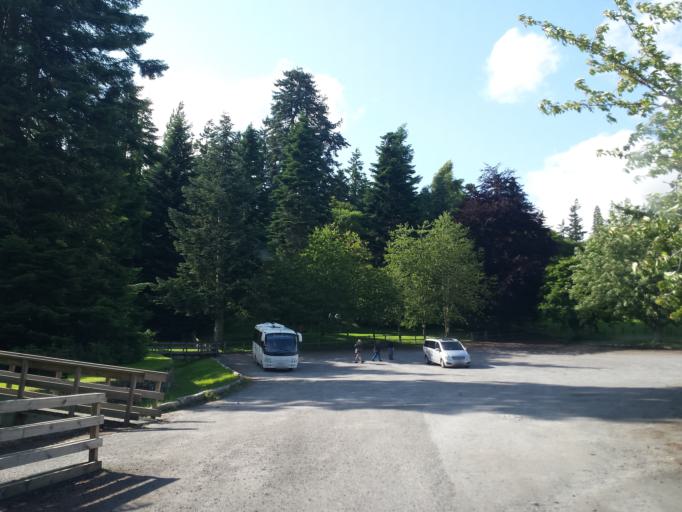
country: GB
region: Scotland
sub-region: Perth and Kinross
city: Pitlochry
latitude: 56.7742
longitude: -3.8555
